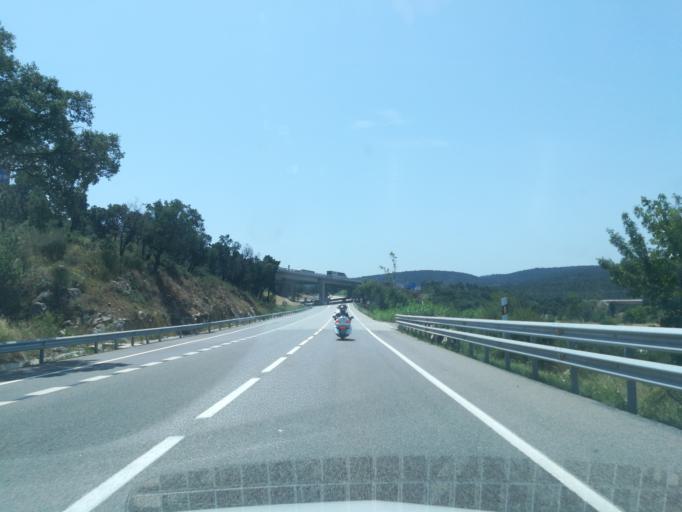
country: ES
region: Catalonia
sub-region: Provincia de Girona
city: la Jonquera
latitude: 42.4398
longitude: 2.8658
